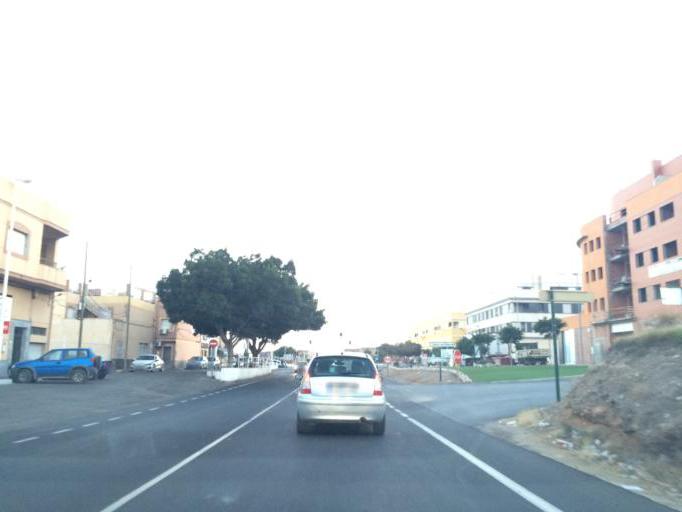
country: ES
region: Andalusia
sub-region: Provincia de Almeria
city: Benahadux
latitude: 36.9241
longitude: -2.4617
